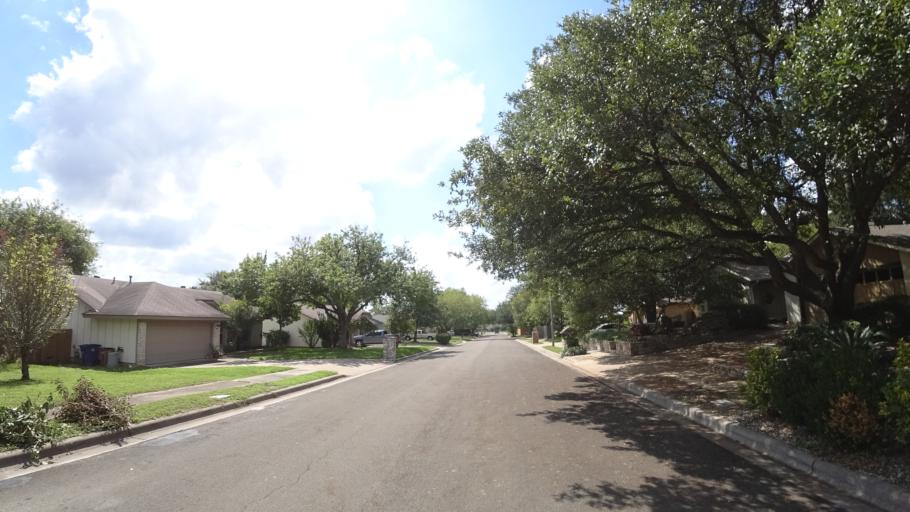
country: US
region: Texas
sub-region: Travis County
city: Onion Creek
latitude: 30.1893
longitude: -97.7831
